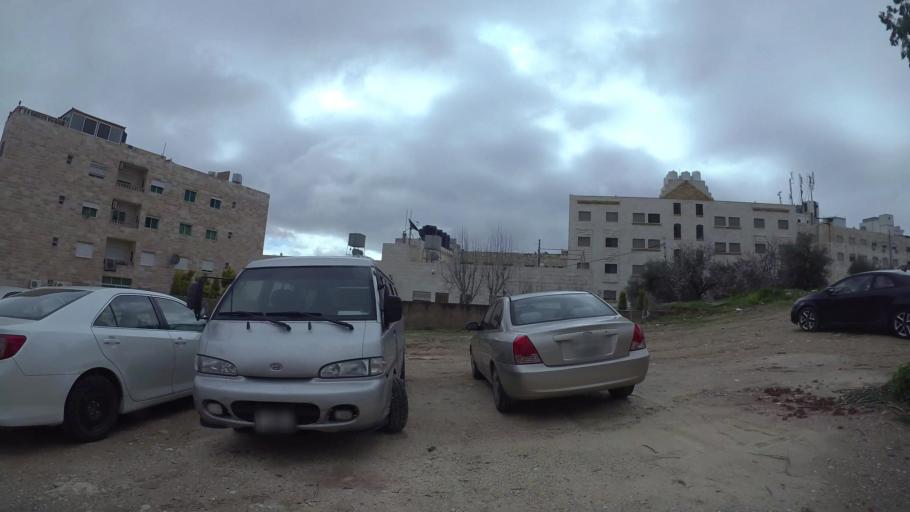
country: JO
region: Amman
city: Al Jubayhah
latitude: 32.0543
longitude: 35.8860
